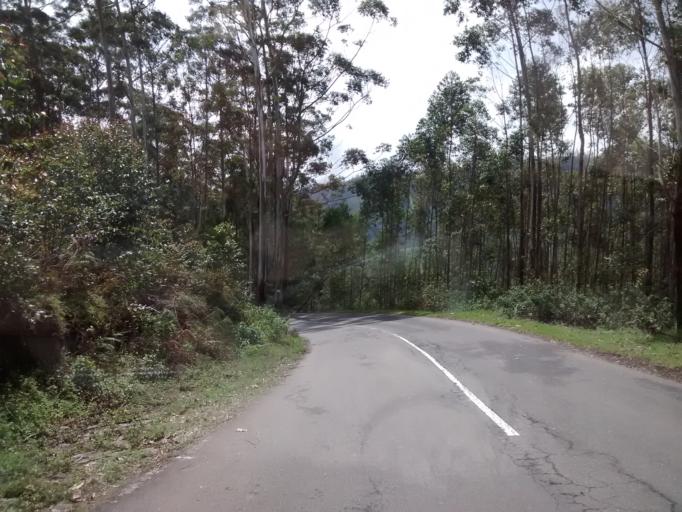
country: IN
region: Kerala
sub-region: Idukki
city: Munnar
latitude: 10.0994
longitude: 77.1099
